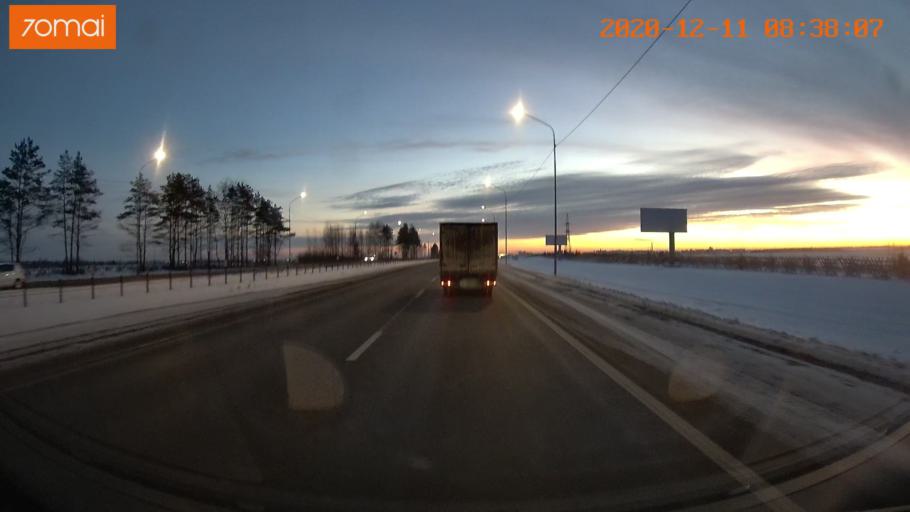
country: RU
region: Vologda
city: Molochnoye
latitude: 59.2120
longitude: 39.7239
